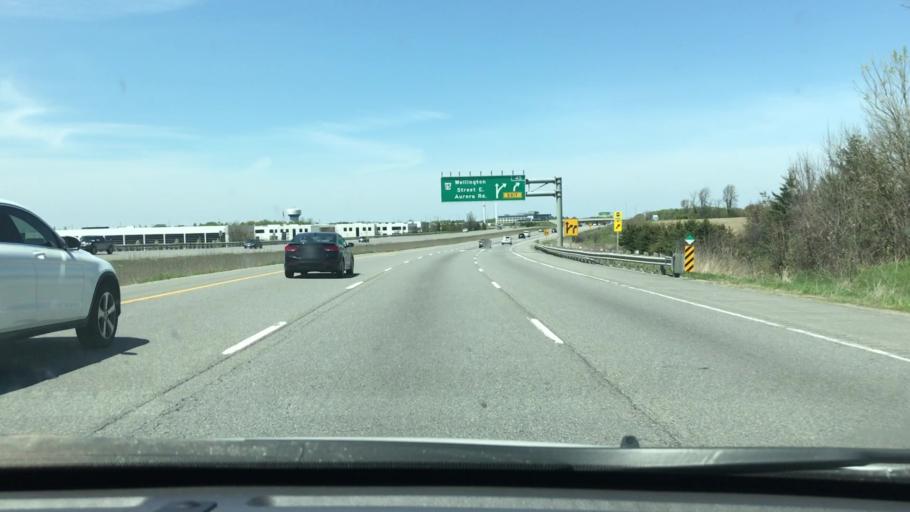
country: CA
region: Ontario
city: Newmarket
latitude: 44.0055
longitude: -79.4041
